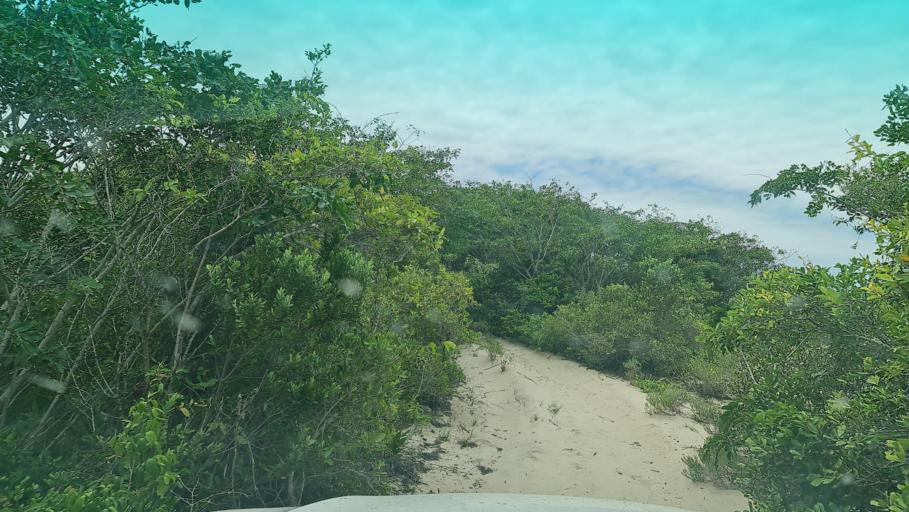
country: MZ
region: Maputo
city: Manhica
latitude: -25.6287
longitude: 32.7885
